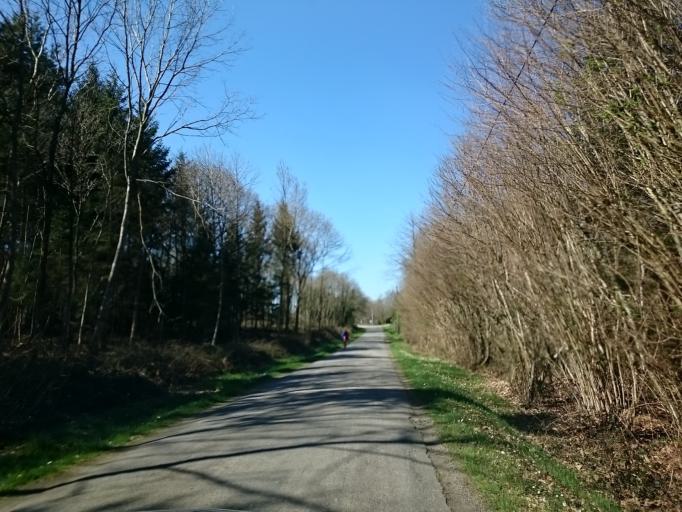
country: FR
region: Brittany
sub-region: Departement d'Ille-et-Vilaine
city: Crevin
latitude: 47.9609
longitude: -1.6723
